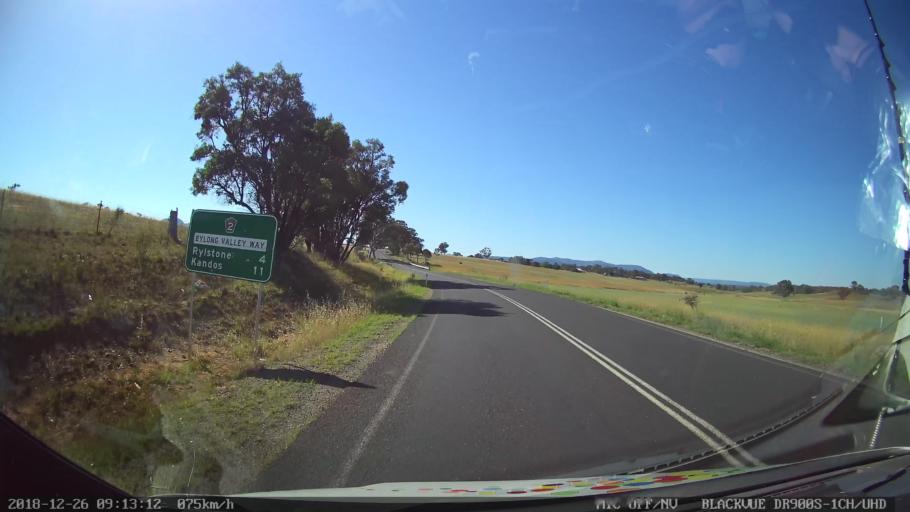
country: AU
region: New South Wales
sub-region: Mid-Western Regional
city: Kandos
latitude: -32.7654
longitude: 149.9776
